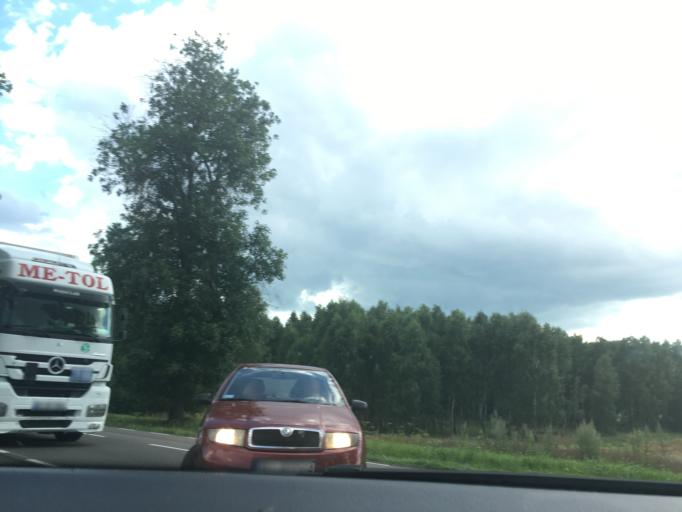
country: PL
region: Podlasie
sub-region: Powiat bielski
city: Bielsk Podlaski
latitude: 52.8226
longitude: 23.1954
